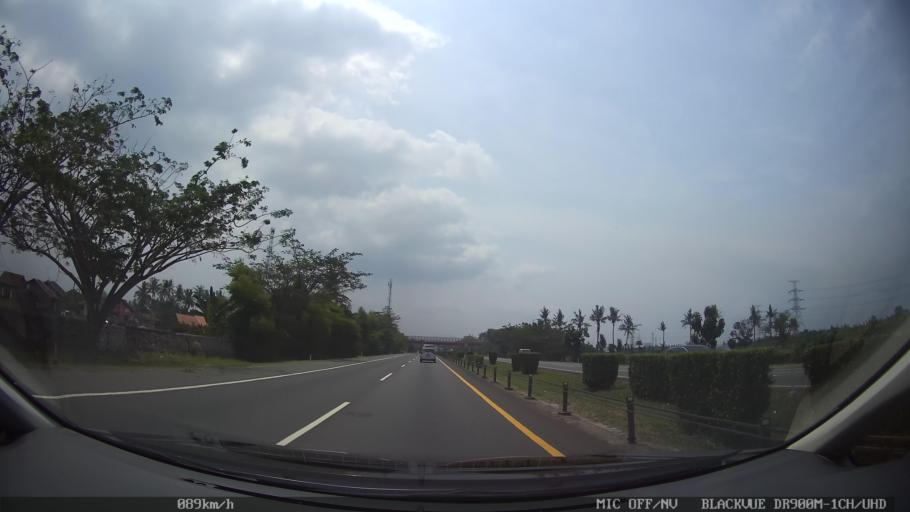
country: ID
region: Banten
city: Bojonegara
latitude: -6.0362
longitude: 106.1023
